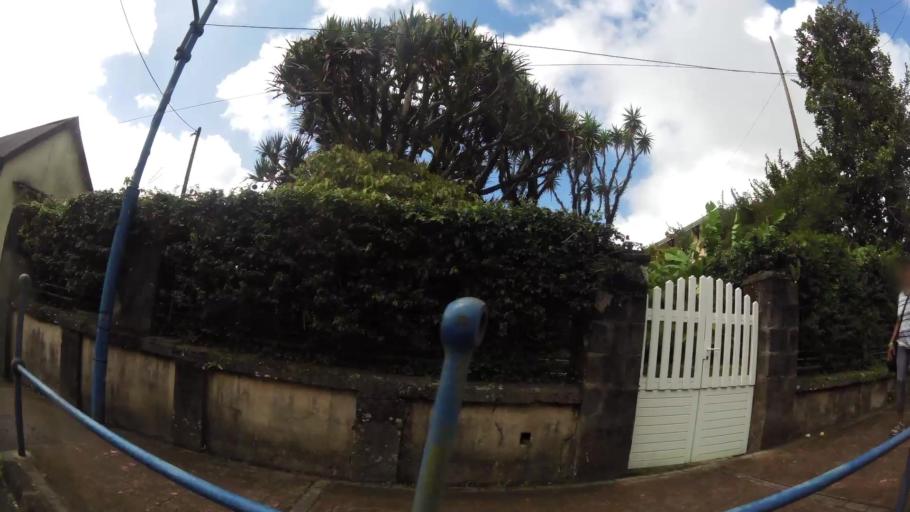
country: MQ
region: Martinique
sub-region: Martinique
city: Le Morne-Rouge
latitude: 14.7725
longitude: -61.1349
